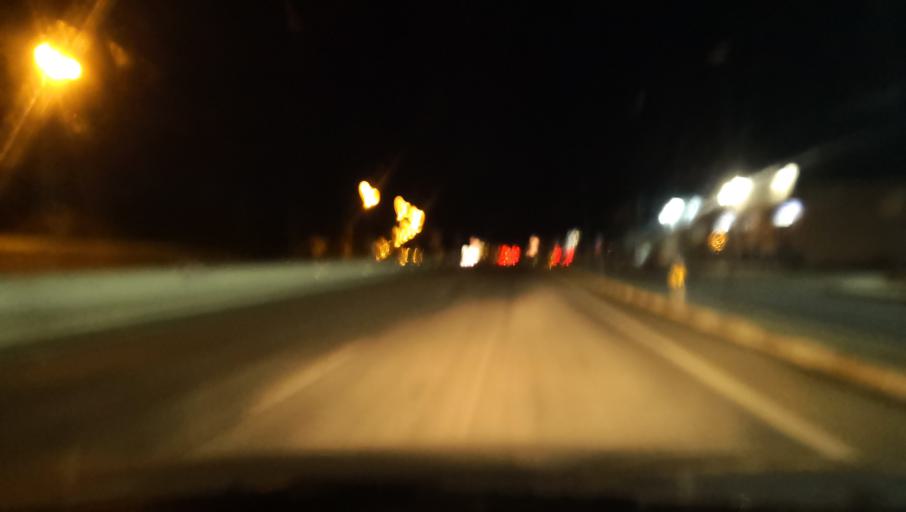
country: ES
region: Castille and Leon
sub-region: Provincia de Zamora
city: Valcabado
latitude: 41.5313
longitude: -5.7597
